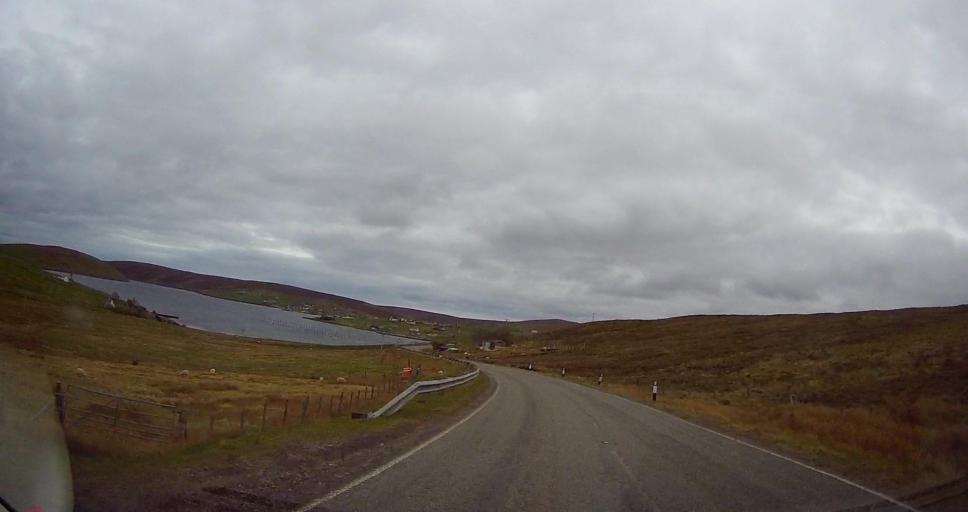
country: GB
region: Scotland
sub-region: Shetland Islands
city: Shetland
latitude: 60.6146
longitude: -1.0748
